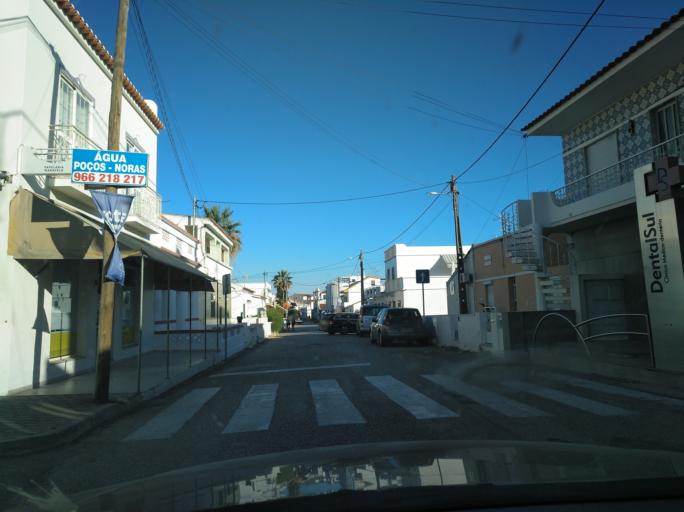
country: PT
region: Faro
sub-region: Vila Real de Santo Antonio
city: Monte Gordo
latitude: 37.1798
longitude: -7.5024
